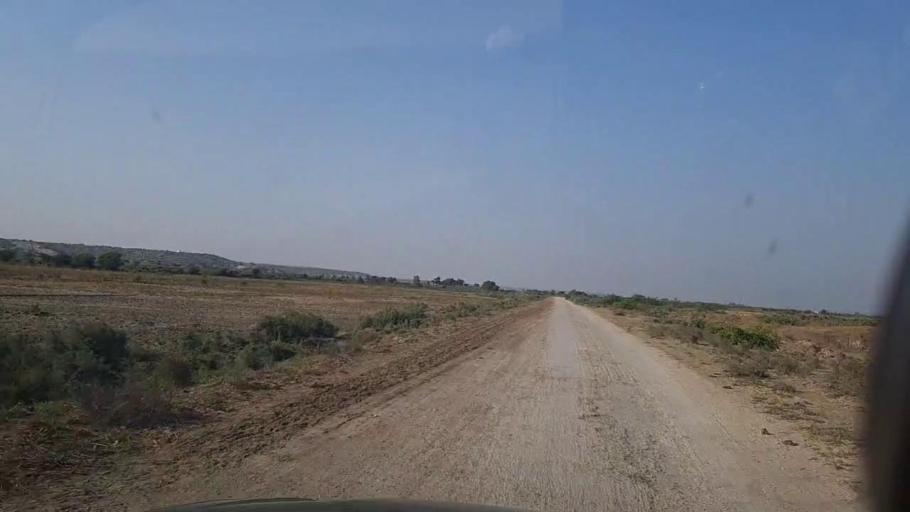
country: PK
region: Sindh
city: Thatta
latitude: 24.5902
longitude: 67.8762
